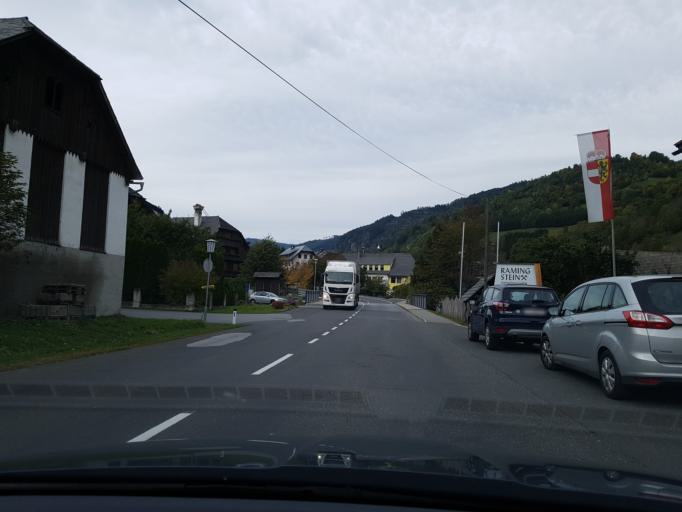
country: AT
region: Salzburg
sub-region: Politischer Bezirk Tamsweg
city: Ramingstein
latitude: 47.0681
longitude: 13.8837
